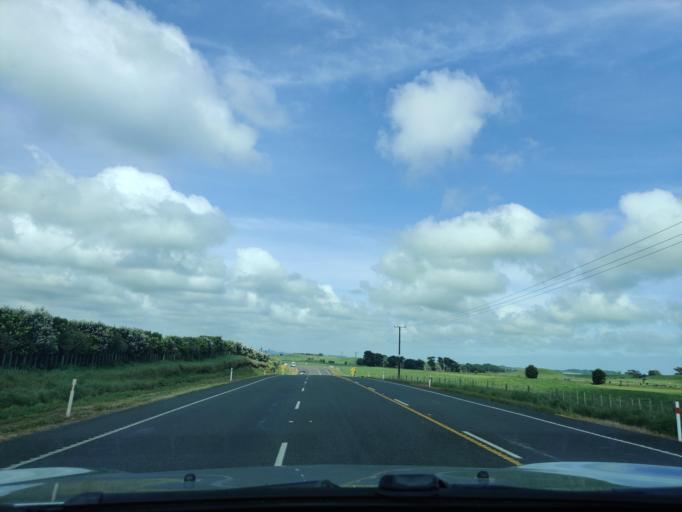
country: NZ
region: Taranaki
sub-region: South Taranaki District
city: Patea
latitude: -39.7676
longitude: 174.6546
